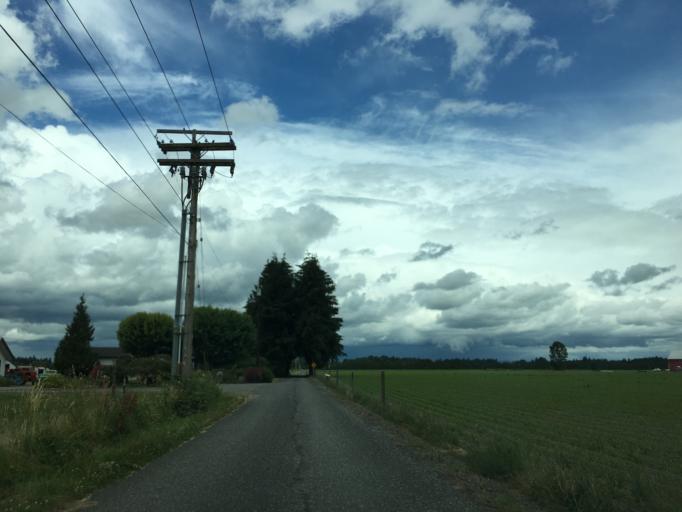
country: US
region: Washington
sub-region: Whatcom County
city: Lynden
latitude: 48.9166
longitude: -122.4965
